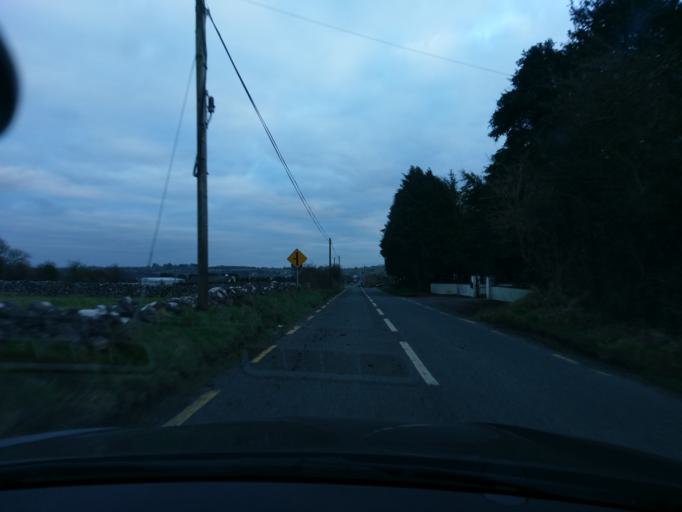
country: IE
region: Connaught
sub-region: County Galway
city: Athenry
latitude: 53.4013
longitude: -8.8042
